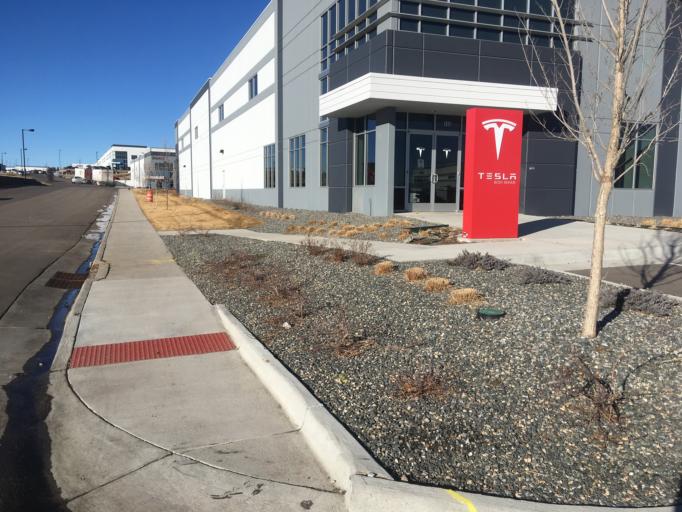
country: US
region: Colorado
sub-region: Adams County
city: Twin Lakes
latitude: 39.7901
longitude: -104.9818
